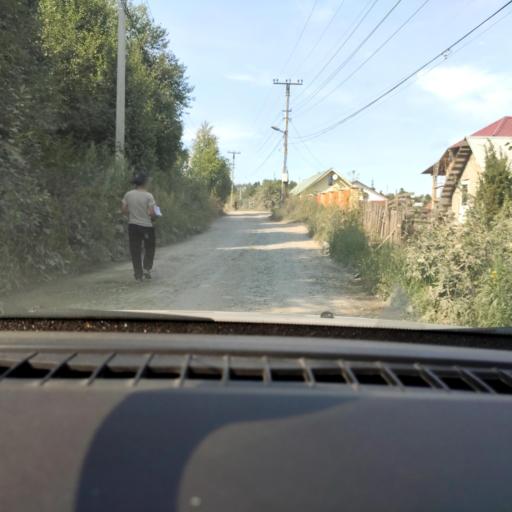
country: RU
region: Perm
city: Polazna
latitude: 58.1415
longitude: 56.4571
